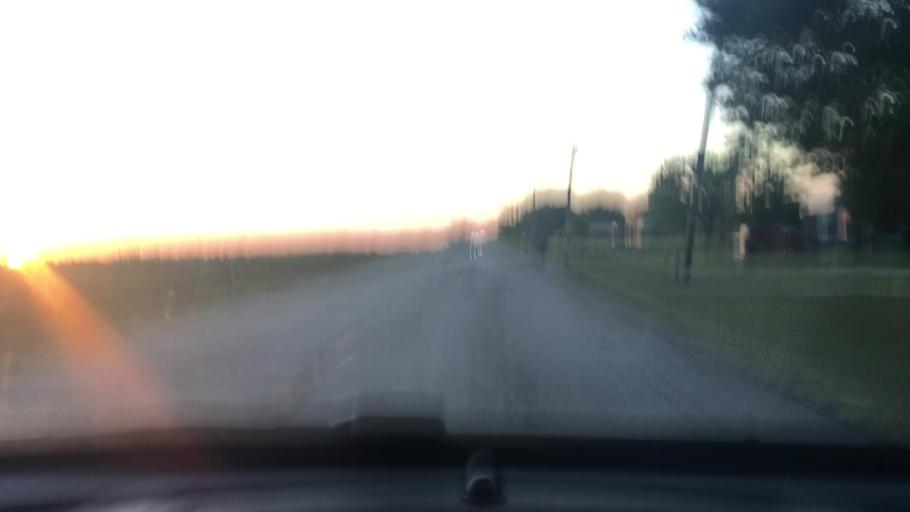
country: US
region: Texas
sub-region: Ellis County
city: Red Oak
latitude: 32.5607
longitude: -96.7965
